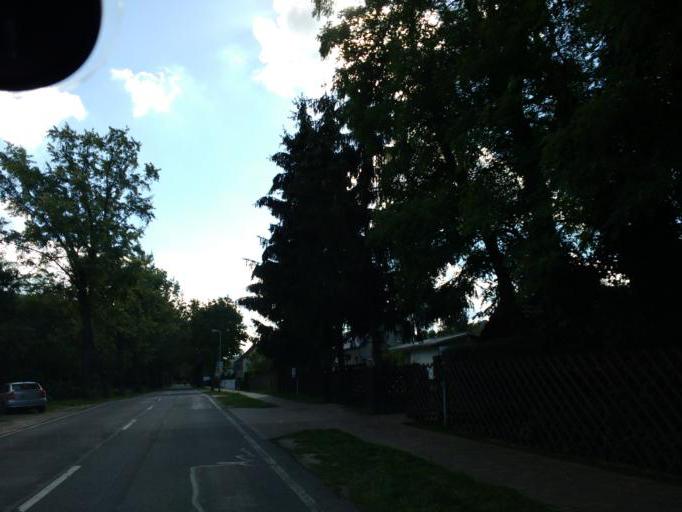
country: DE
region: Brandenburg
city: Mittenwalde
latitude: 52.2173
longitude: 13.5823
